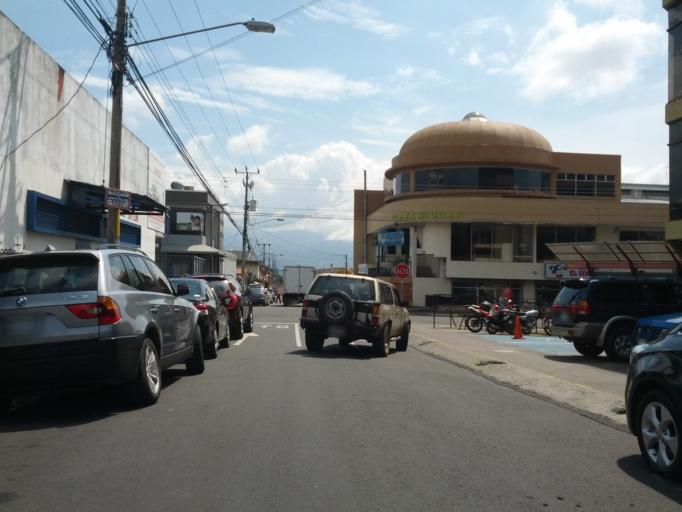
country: CR
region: Alajuela
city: Alajuela
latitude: 10.0175
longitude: -84.2101
